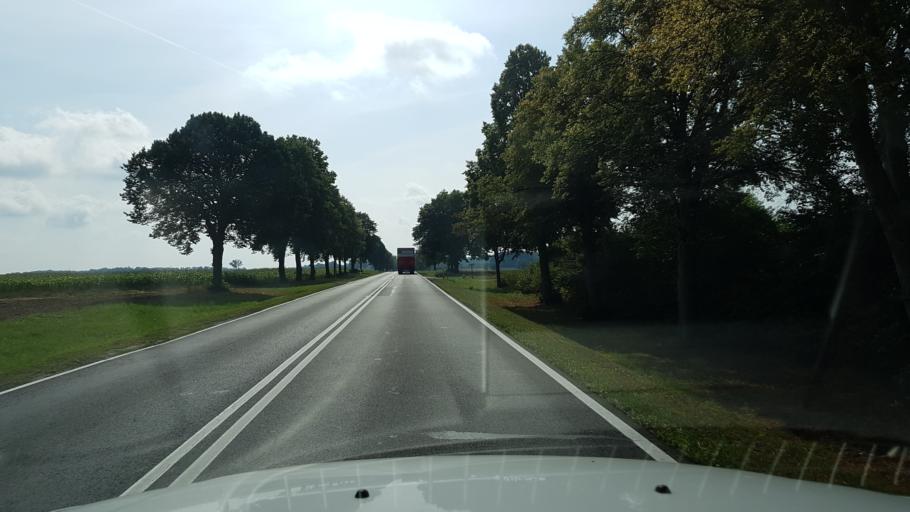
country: PL
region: West Pomeranian Voivodeship
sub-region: Powiat walecki
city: Walcz
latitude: 53.3273
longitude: 16.3046
